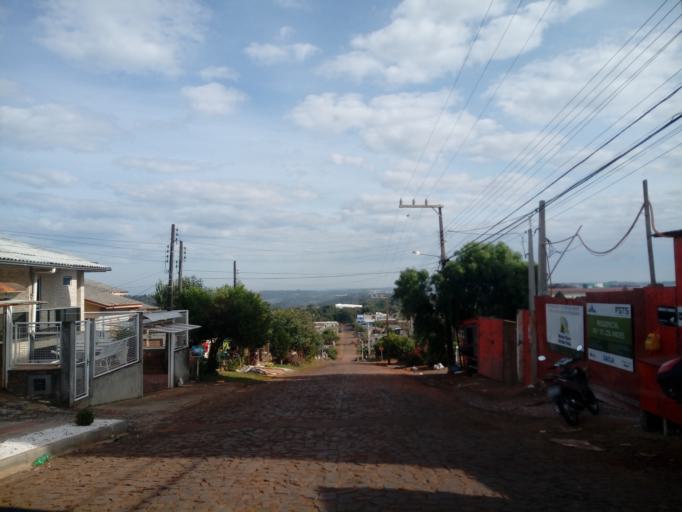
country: BR
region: Santa Catarina
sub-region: Chapeco
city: Chapeco
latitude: -27.1215
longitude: -52.6263
